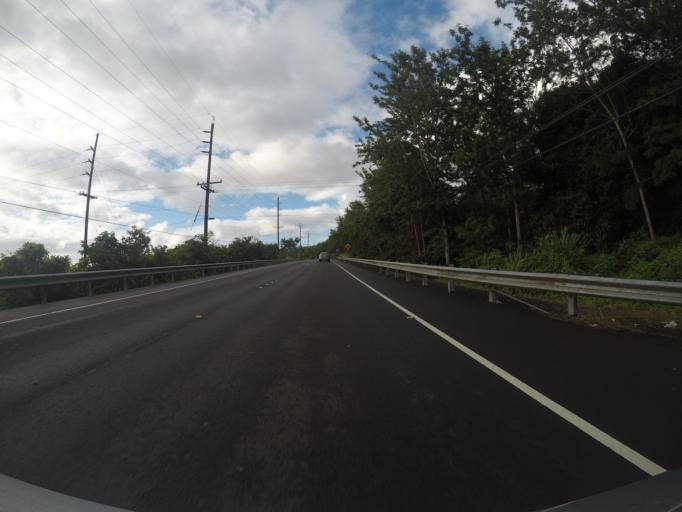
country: US
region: Hawaii
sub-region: Hawaii County
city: Kalaoa
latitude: 19.7416
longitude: -155.9757
